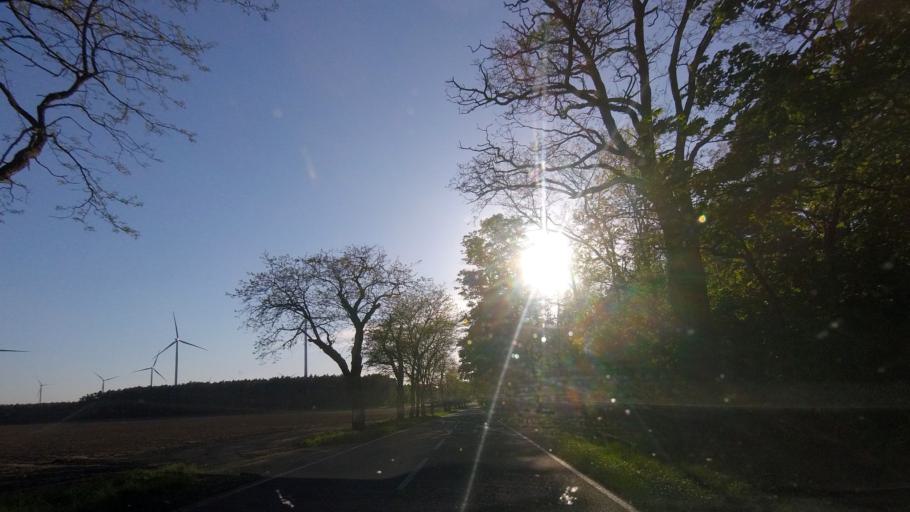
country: DE
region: Brandenburg
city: Ihlow
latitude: 51.9860
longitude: 13.3335
